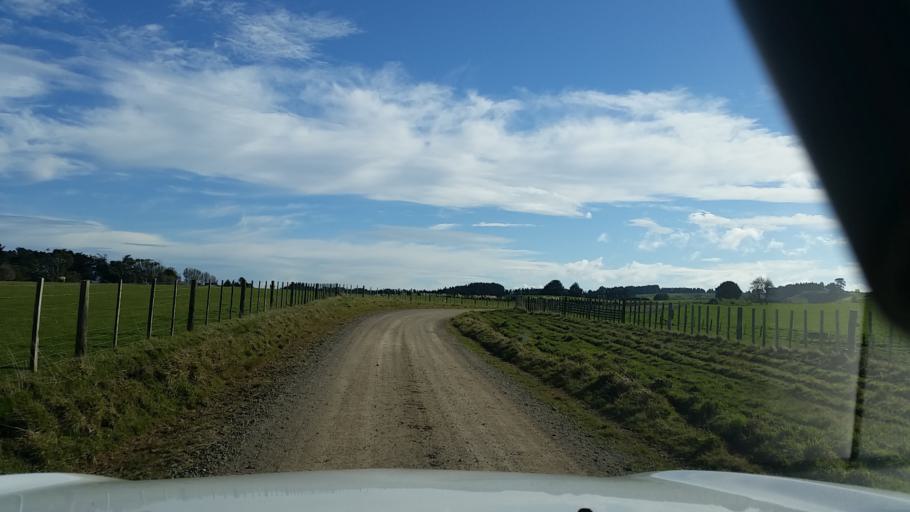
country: NZ
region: Taranaki
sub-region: South Taranaki District
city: Patea
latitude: -39.7046
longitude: 174.6345
